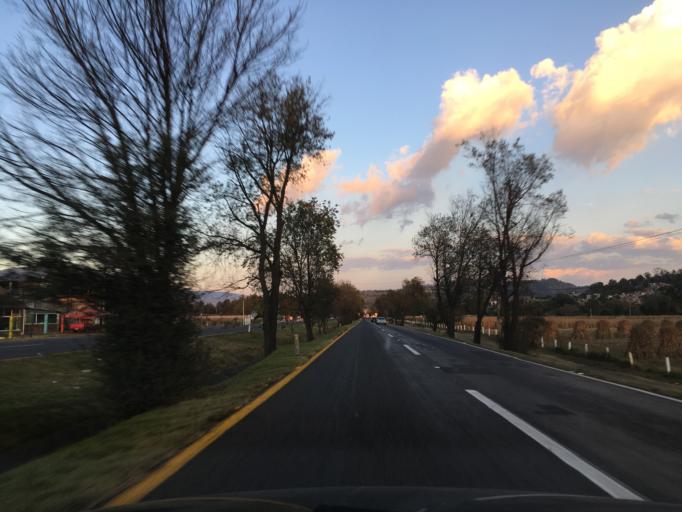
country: MX
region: Michoacan
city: Huiramba
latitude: 19.5450
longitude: -101.4492
